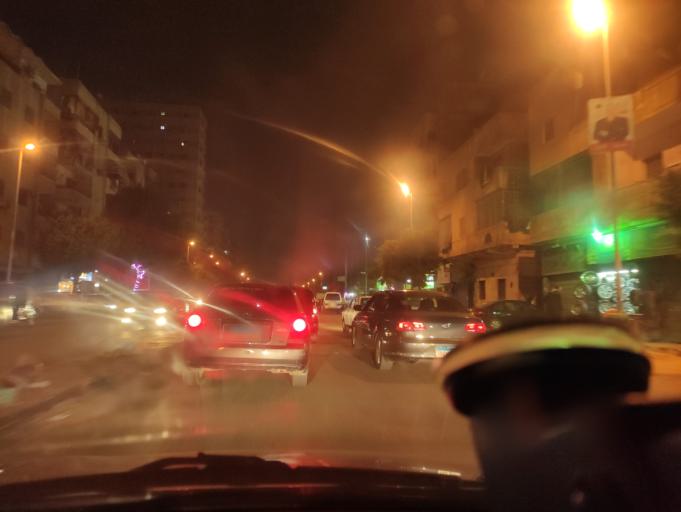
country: EG
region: Muhafazat al Qahirah
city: Cairo
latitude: 30.0915
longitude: 31.2803
